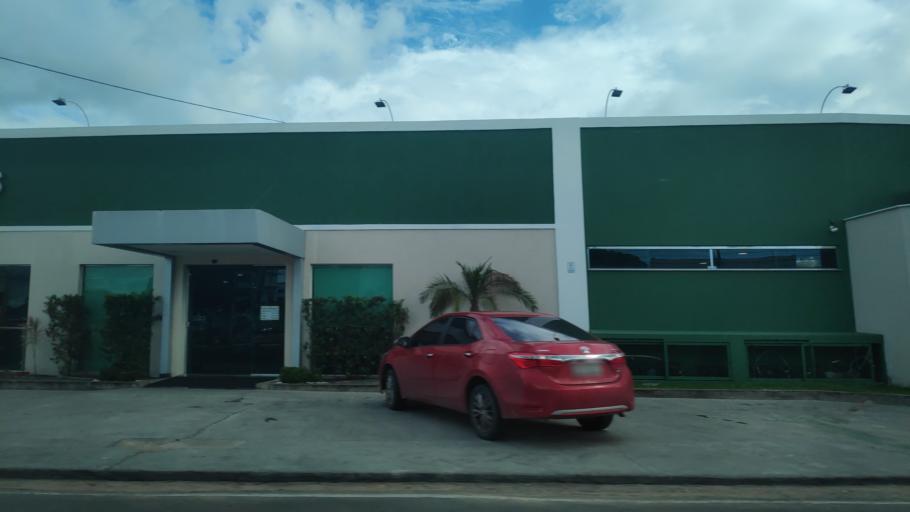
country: BR
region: Roraima
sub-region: Boa Vista
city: Boa Vista
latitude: 2.8286
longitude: -60.6713
